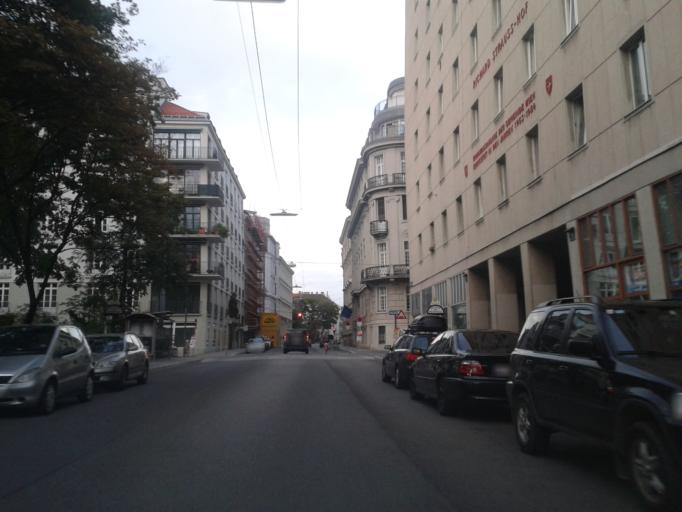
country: AT
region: Vienna
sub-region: Wien Stadt
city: Vienna
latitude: 48.1991
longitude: 16.3823
